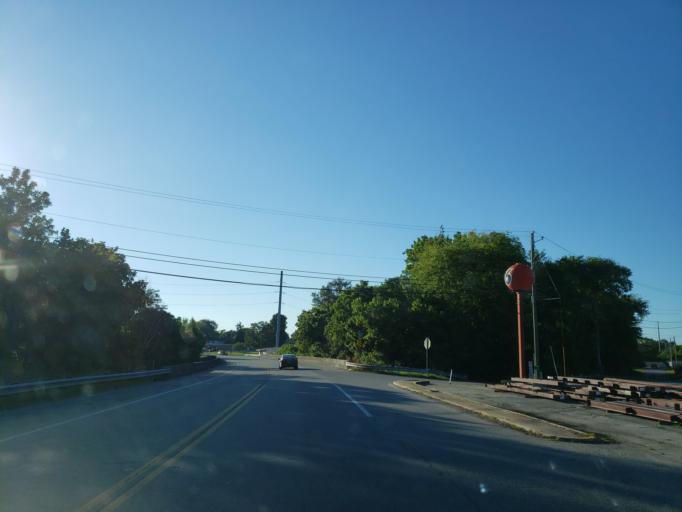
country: US
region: Georgia
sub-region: Polk County
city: Aragon
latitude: 34.0383
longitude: -85.0531
